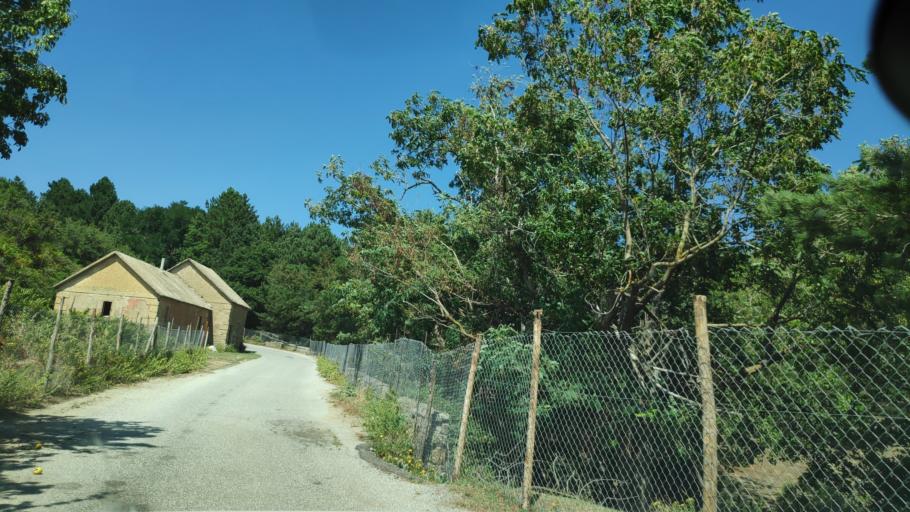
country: IT
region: Calabria
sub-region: Provincia di Reggio Calabria
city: Bova
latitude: 38.0167
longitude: 15.9348
